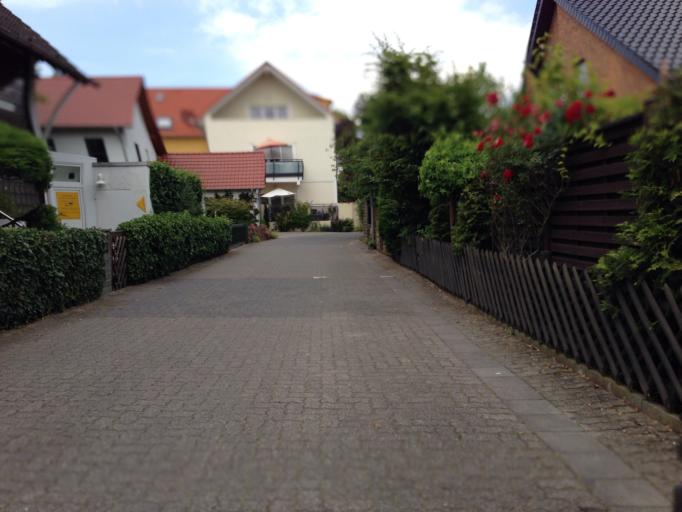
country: DE
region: Hesse
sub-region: Regierungsbezirk Darmstadt
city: Hanau am Main
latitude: 50.1296
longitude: 8.8921
